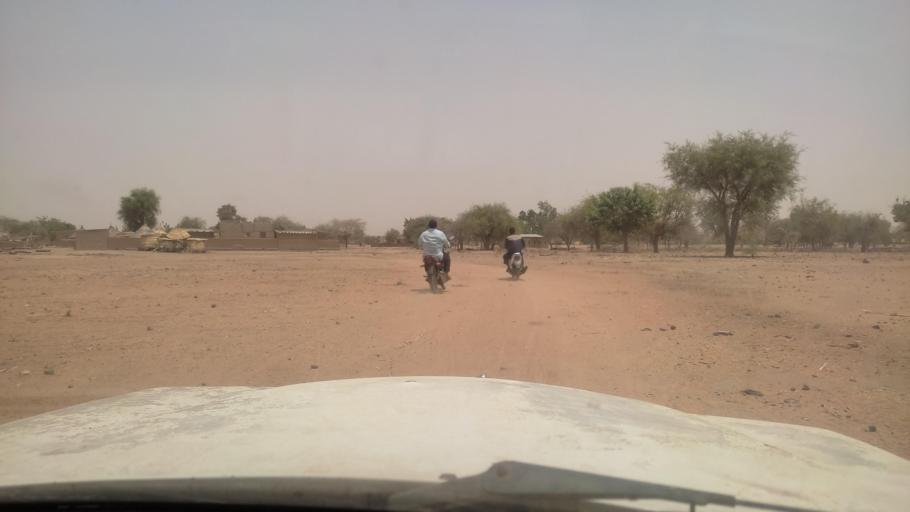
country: BF
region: Est
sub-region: Gnagna Province
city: Bogande
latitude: 13.0065
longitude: -0.0907
